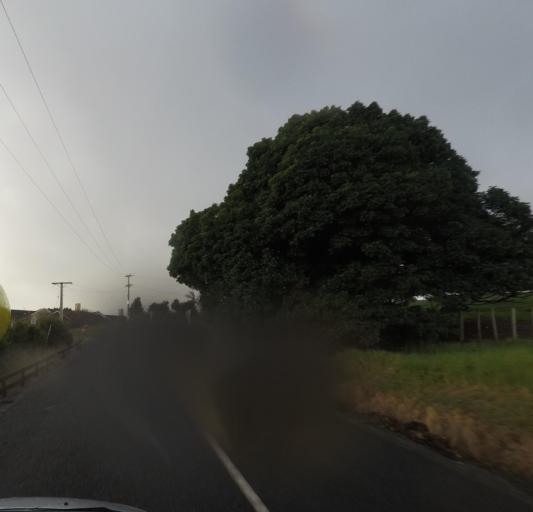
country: NZ
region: Auckland
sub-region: Auckland
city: Warkworth
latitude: -36.3764
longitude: 174.7599
